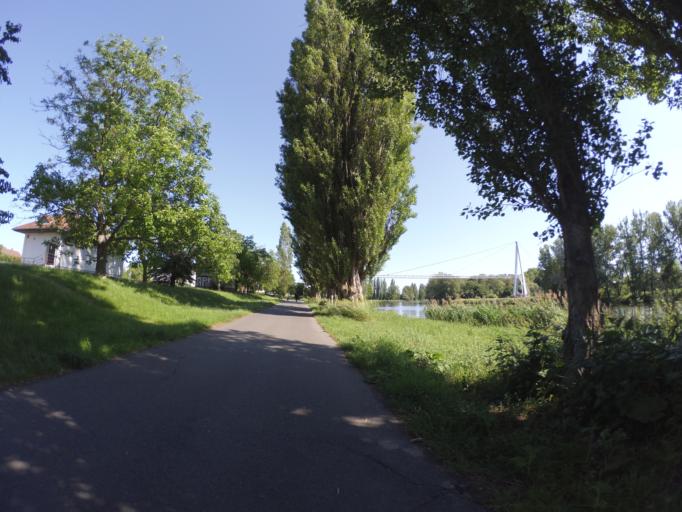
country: CZ
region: Central Bohemia
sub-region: Okres Nymburk
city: Podebrady
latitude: 50.1591
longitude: 15.1040
